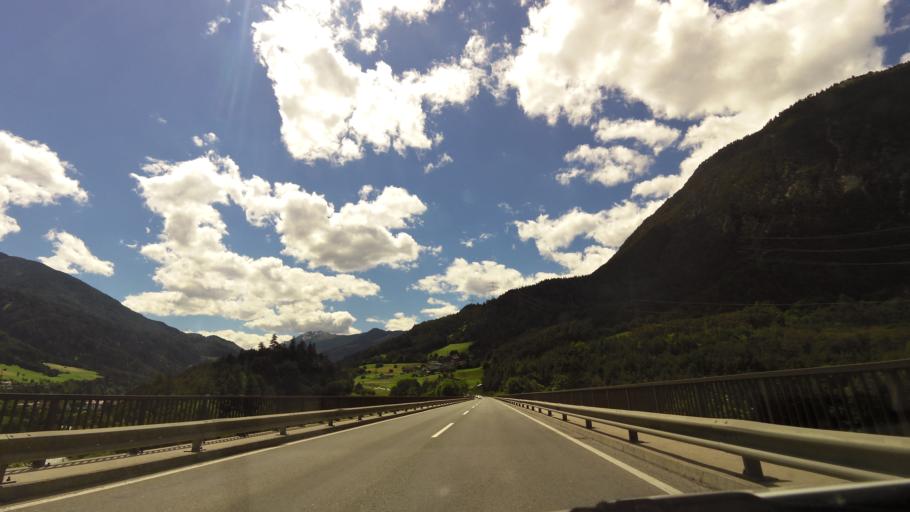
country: AT
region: Tyrol
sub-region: Politischer Bezirk Imst
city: Roppen
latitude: 47.2240
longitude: 10.8218
